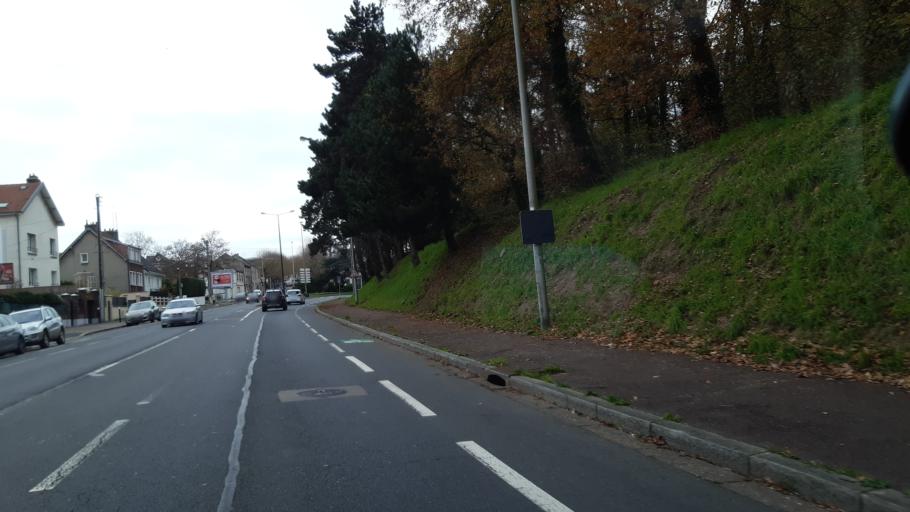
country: FR
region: Haute-Normandie
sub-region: Departement de la Seine-Maritime
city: Fontaine-la-Mallet
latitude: 49.5135
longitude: 0.1520
